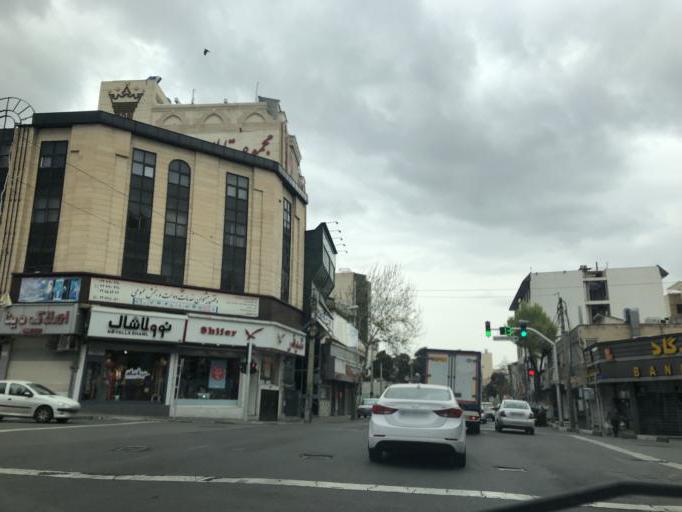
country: IR
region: Tehran
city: Tajrish
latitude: 35.7804
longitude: 51.4534
